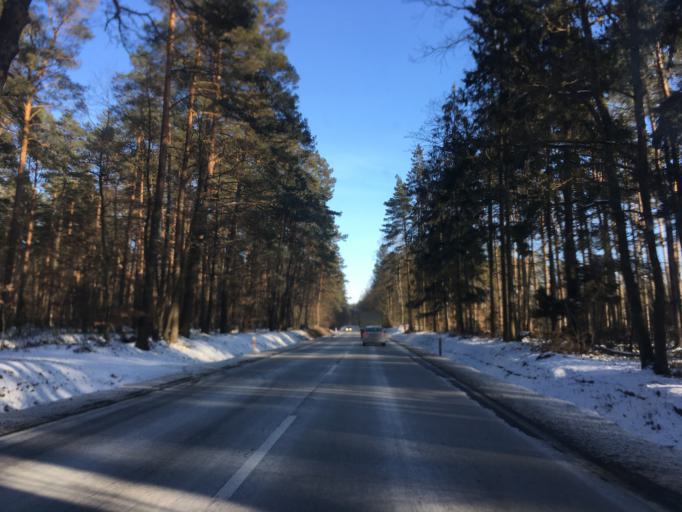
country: PL
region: Pomeranian Voivodeship
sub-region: Powiat koscierski
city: Koscierzyna
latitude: 54.1131
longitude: 17.9099
